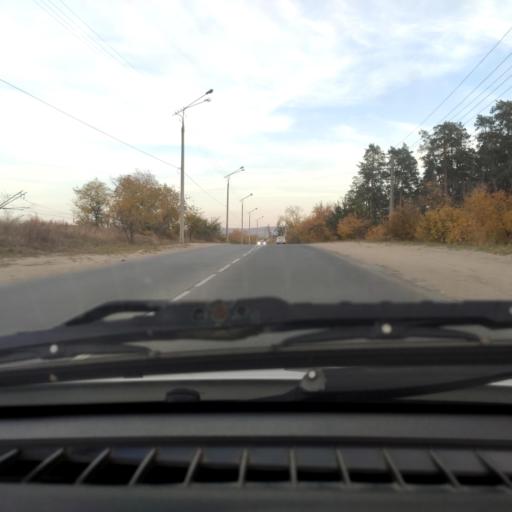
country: RU
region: Samara
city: Zhigulevsk
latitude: 53.4707
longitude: 49.5439
